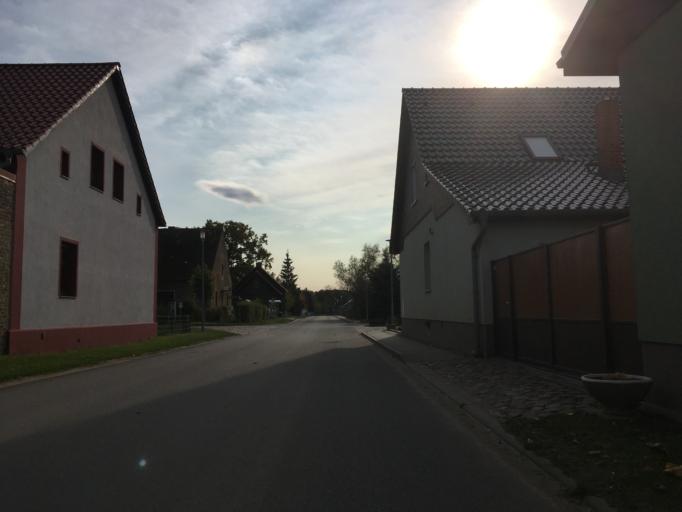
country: DE
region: Brandenburg
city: Templin
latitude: 53.0249
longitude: 13.4796
